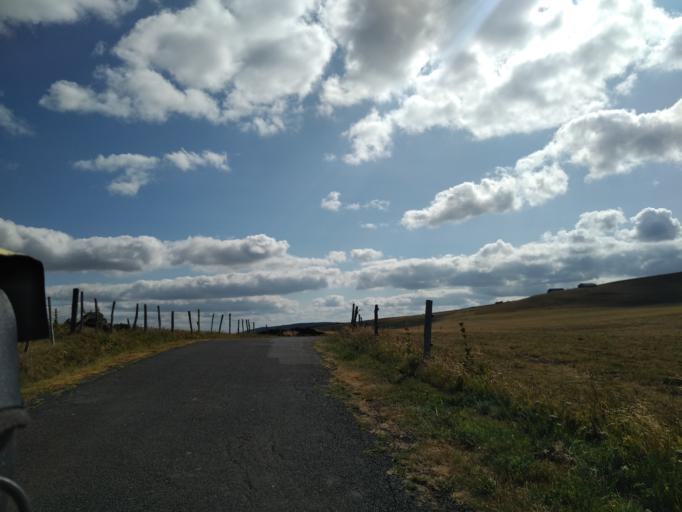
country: FR
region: Auvergne
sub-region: Departement du Cantal
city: Murat
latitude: 45.0258
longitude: 2.8212
